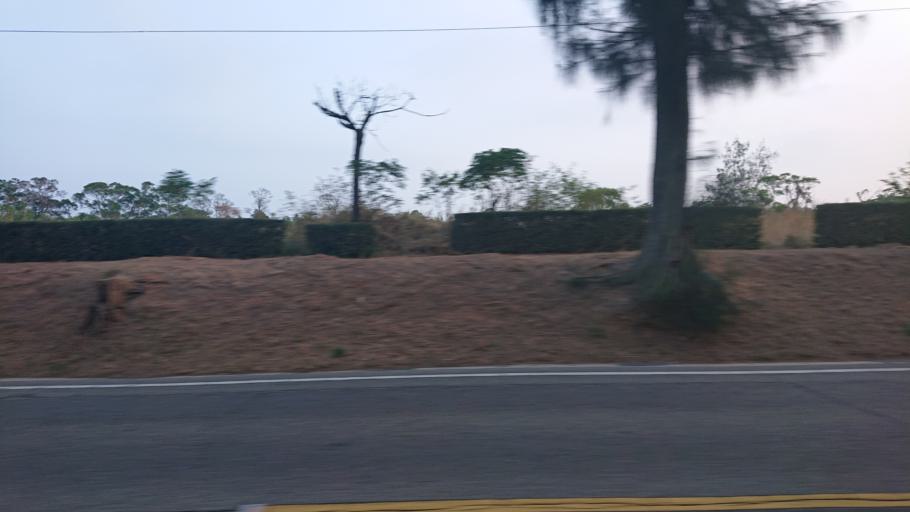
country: TW
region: Fukien
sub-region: Kinmen
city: Jincheng
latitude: 24.4540
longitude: 118.3607
